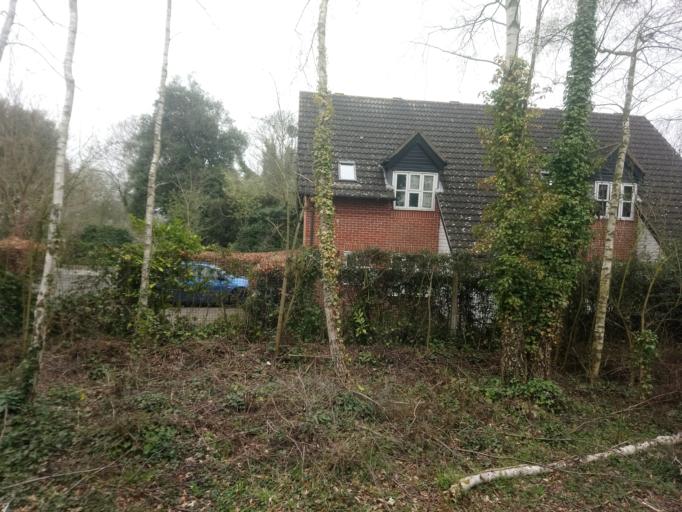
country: GB
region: England
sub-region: Suffolk
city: Leiston
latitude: 52.2103
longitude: 1.5717
